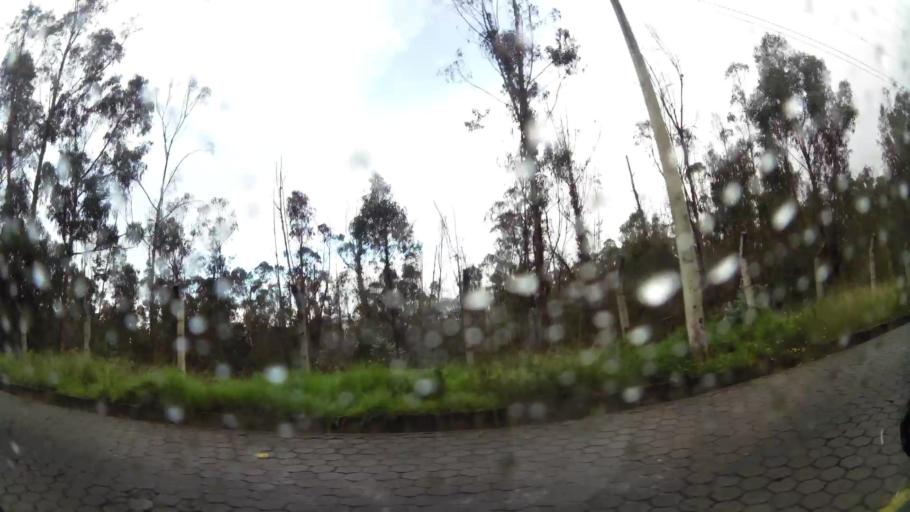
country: EC
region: Pichincha
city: Quito
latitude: -0.0913
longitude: -78.4973
